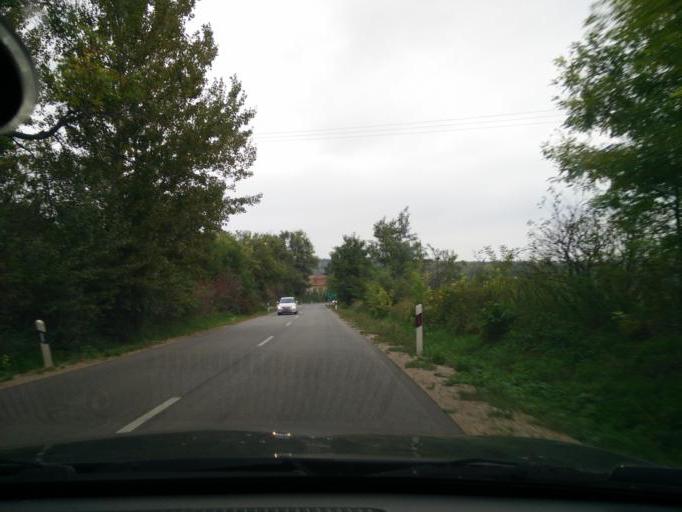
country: HU
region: Komarom-Esztergom
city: Tokod
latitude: 47.6984
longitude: 18.6174
